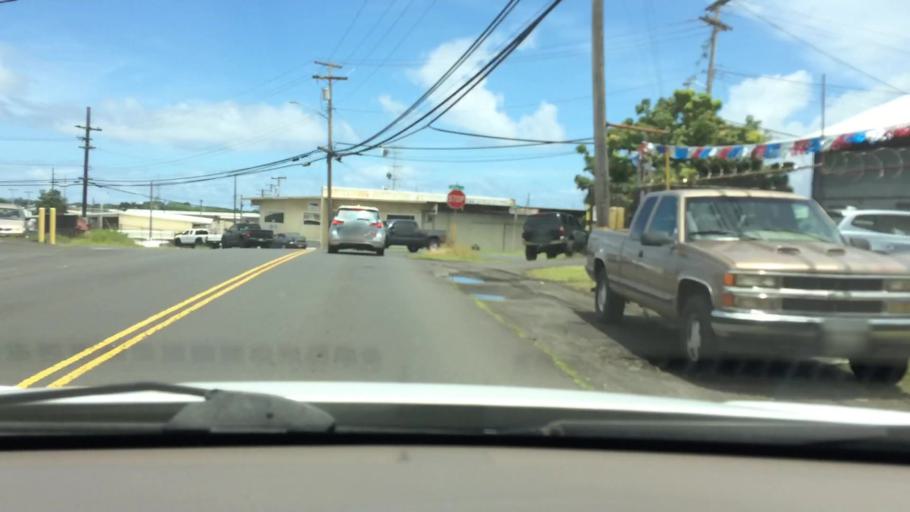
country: US
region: Hawaii
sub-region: Hawaii County
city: Hilo
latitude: 19.7021
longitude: -155.0626
